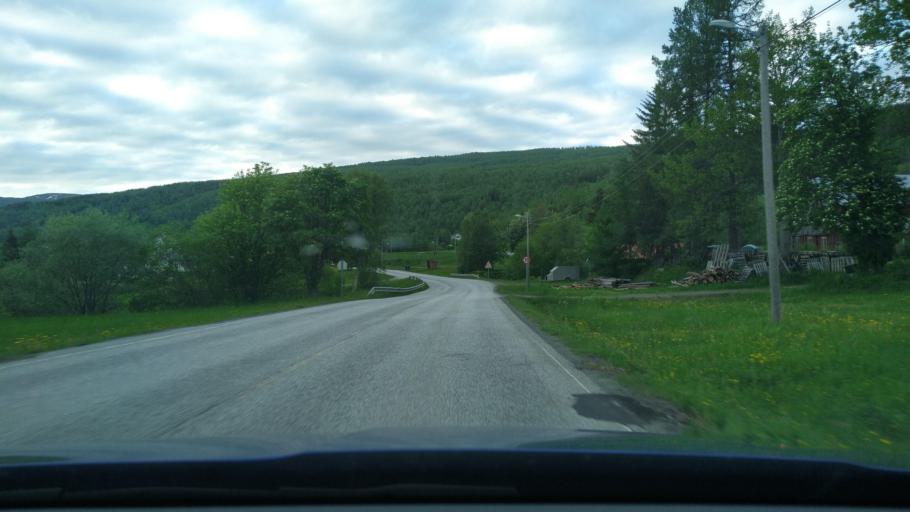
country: NO
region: Troms
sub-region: Sorreisa
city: Sorreisa
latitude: 69.1176
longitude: 18.2167
